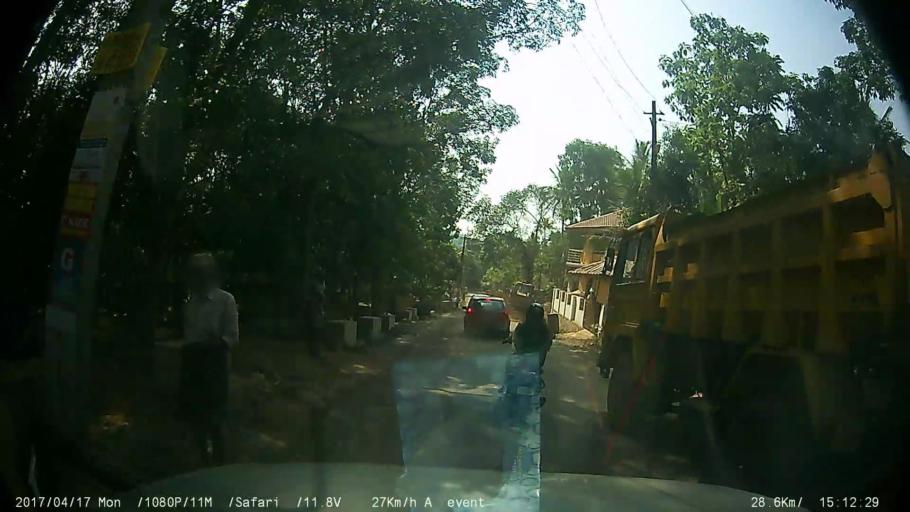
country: IN
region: Kerala
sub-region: Ernakulam
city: Piravam
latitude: 9.8961
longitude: 76.4800
